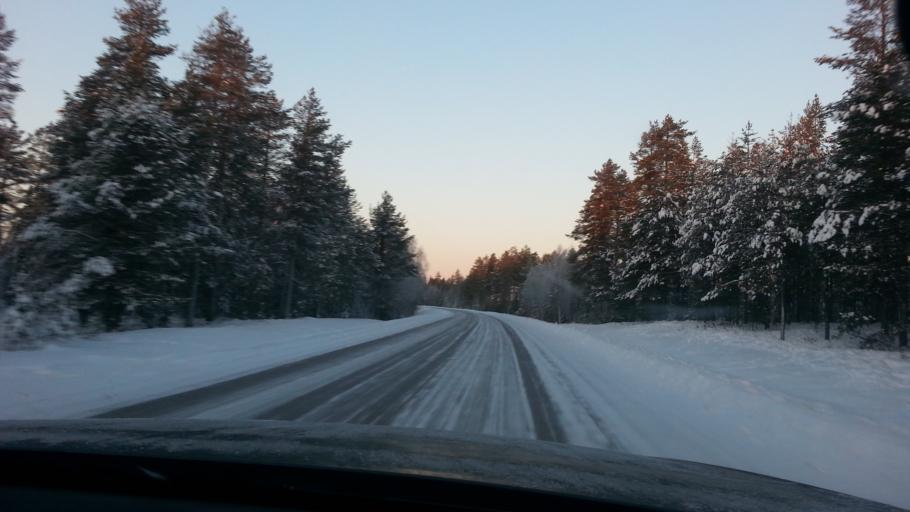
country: FI
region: Lapland
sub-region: Rovaniemi
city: Rovaniemi
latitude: 66.7739
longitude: 25.4587
